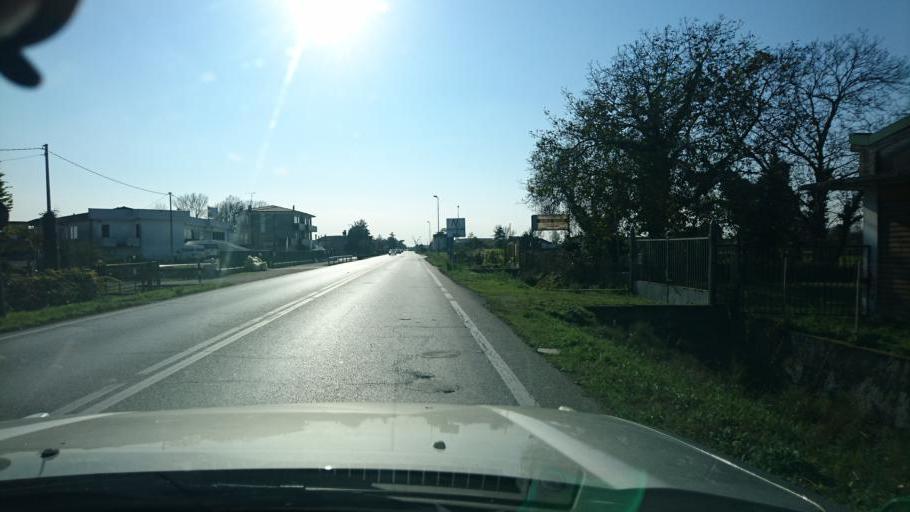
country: IT
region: Veneto
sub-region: Provincia di Padova
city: Monselice
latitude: 45.2220
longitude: 11.7551
